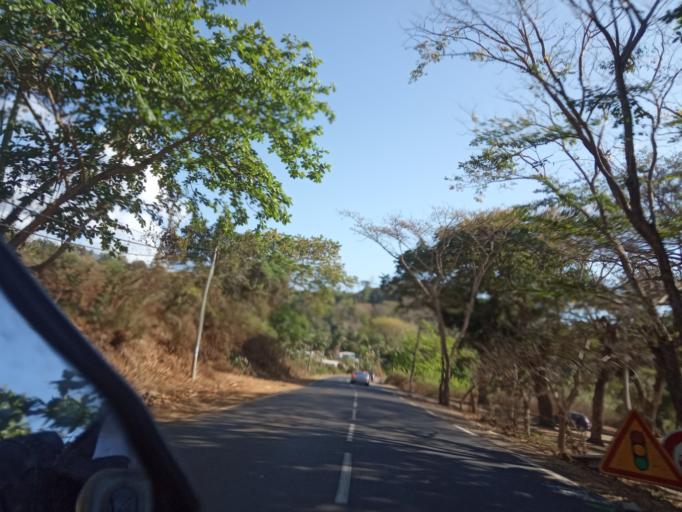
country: YT
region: Bandrele
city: Bandrele
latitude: -12.9196
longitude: 45.1838
